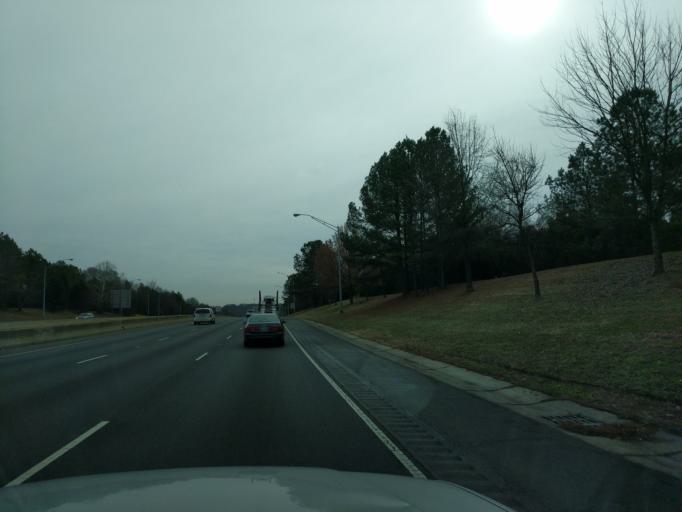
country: US
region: North Carolina
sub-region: Mecklenburg County
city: Charlotte
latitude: 35.2168
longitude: -80.8110
